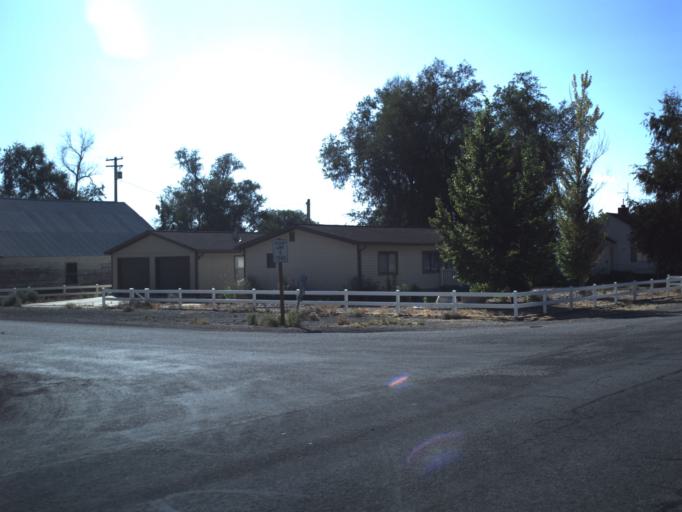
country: US
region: Utah
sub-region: Millard County
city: Delta
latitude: 39.2869
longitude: -112.6528
